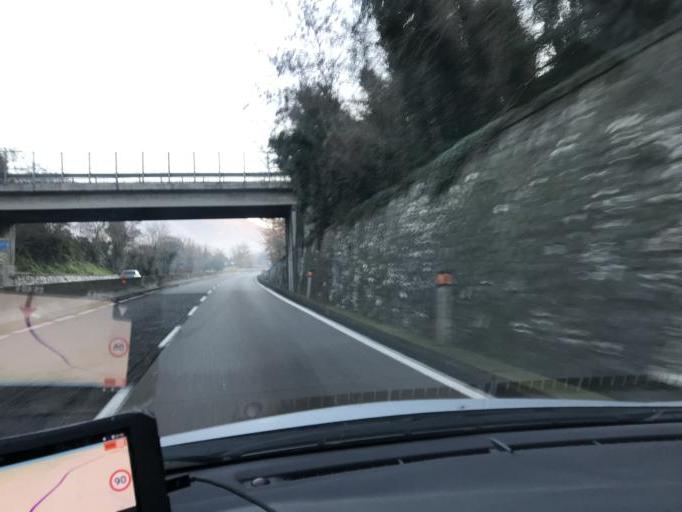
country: IT
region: Umbria
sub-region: Provincia di Terni
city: Terni
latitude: 42.5824
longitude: 12.6406
